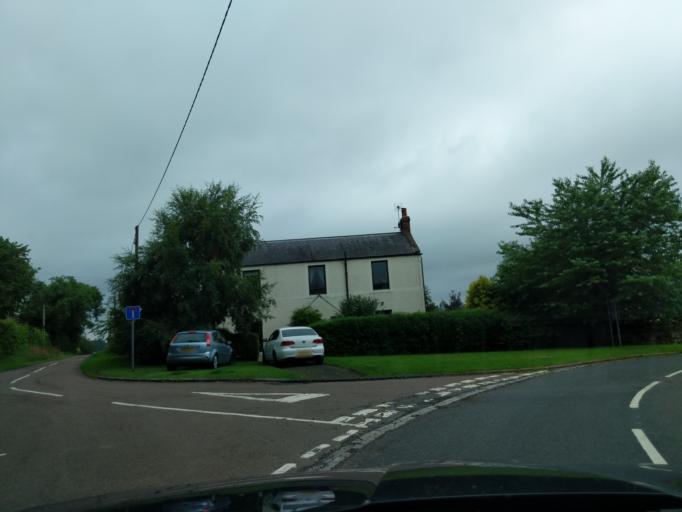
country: GB
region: Scotland
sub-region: The Scottish Borders
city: Allanton
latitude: 55.7163
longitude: -2.1684
